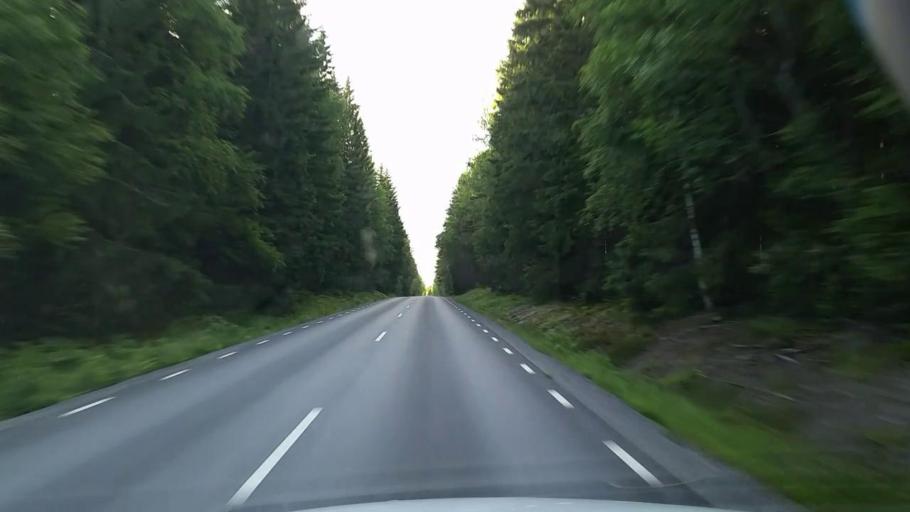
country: SE
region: Vaestmanland
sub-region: Kopings Kommun
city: Kolsva
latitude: 59.6827
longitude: 15.8397
